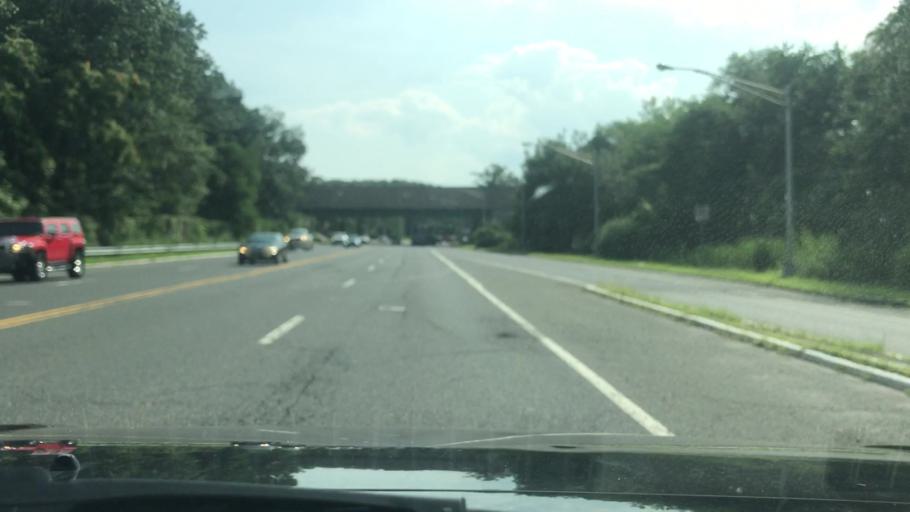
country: US
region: New Jersey
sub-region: Monmouth County
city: Eatontown
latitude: 40.2779
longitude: -74.0706
